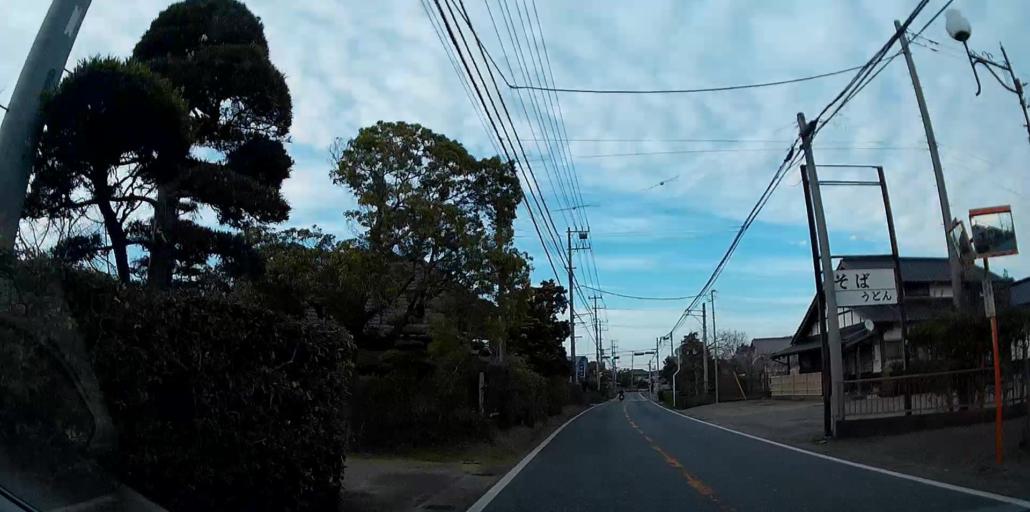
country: JP
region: Chiba
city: Kisarazu
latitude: 35.3697
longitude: 140.0598
